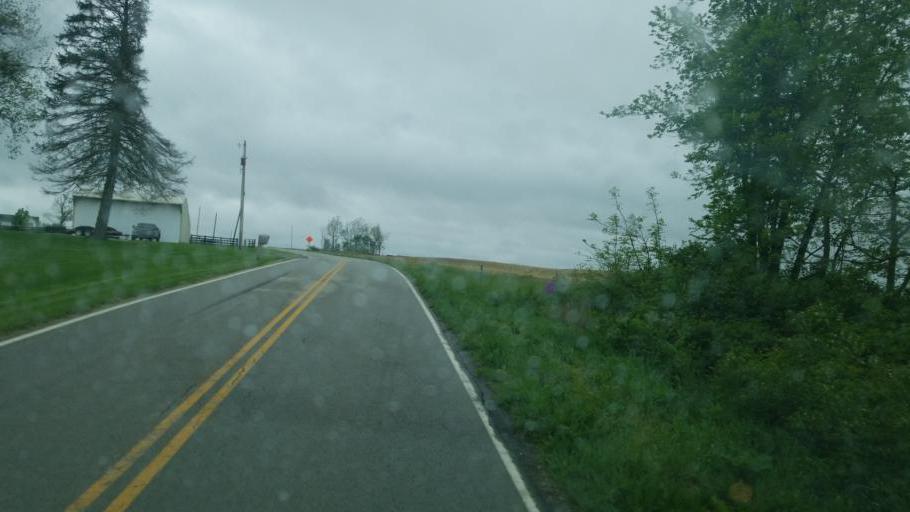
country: US
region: Ohio
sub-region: Highland County
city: Leesburg
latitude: 39.3020
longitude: -83.5785
